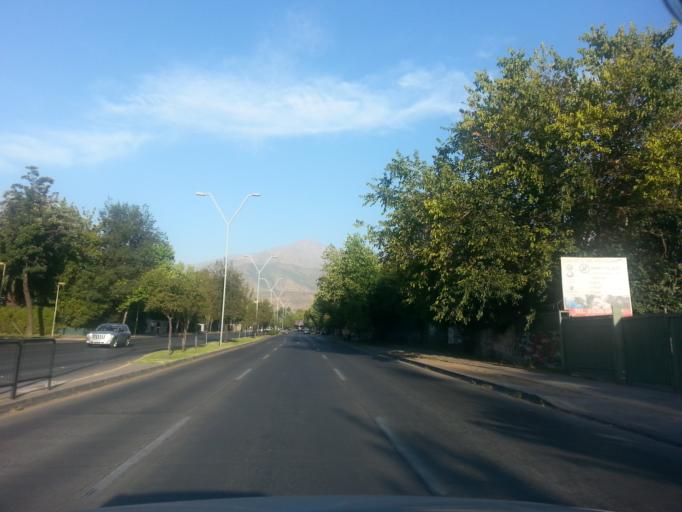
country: CL
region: Santiago Metropolitan
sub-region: Provincia de Santiago
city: Villa Presidente Frei, Nunoa, Santiago, Chile
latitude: -33.4308
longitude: -70.5594
